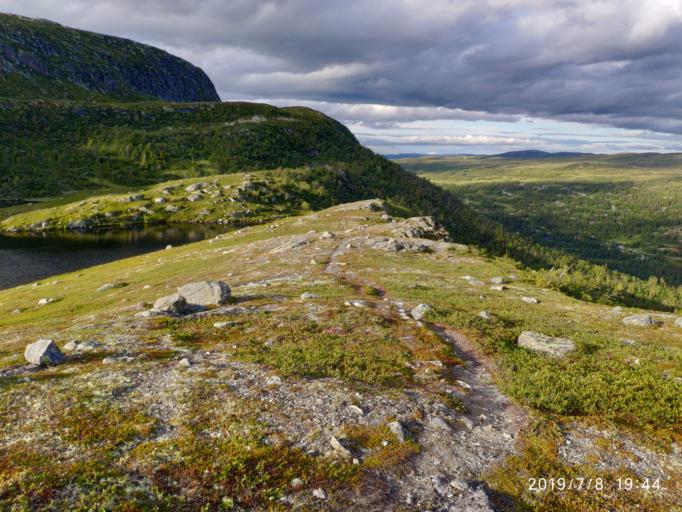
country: NO
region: Buskerud
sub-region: Nes
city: Nesbyen
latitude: 60.3487
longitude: 9.1702
